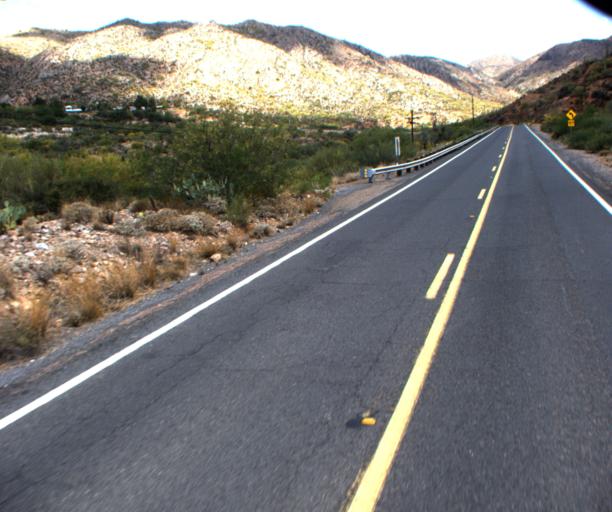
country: US
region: Arizona
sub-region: Pinal County
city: Superior
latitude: 33.1891
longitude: -111.0445
